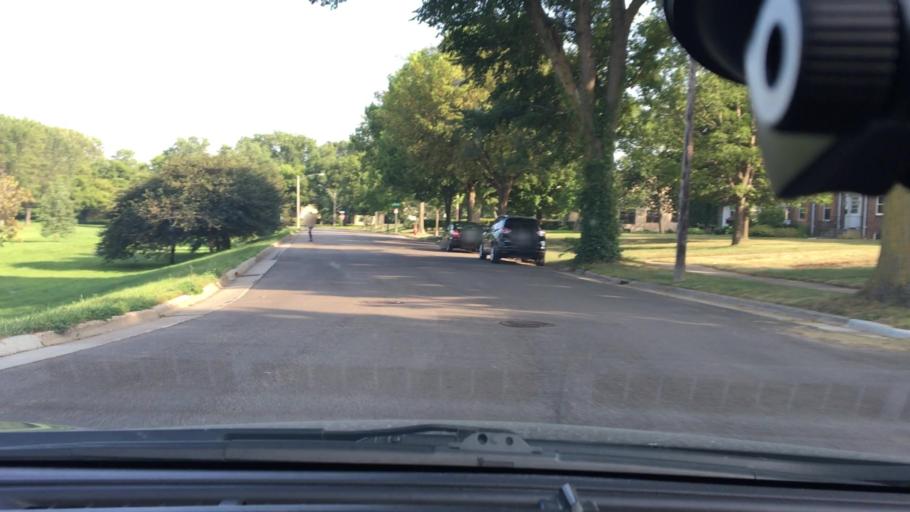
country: US
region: Minnesota
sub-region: Hennepin County
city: Richfield
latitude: 44.9027
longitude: -93.2525
